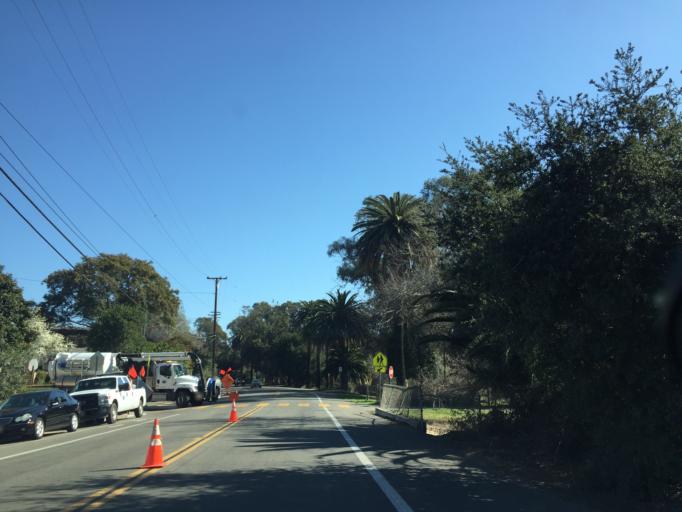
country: US
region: California
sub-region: Santa Barbara County
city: Mission Canyon
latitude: 34.4384
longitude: -119.7670
